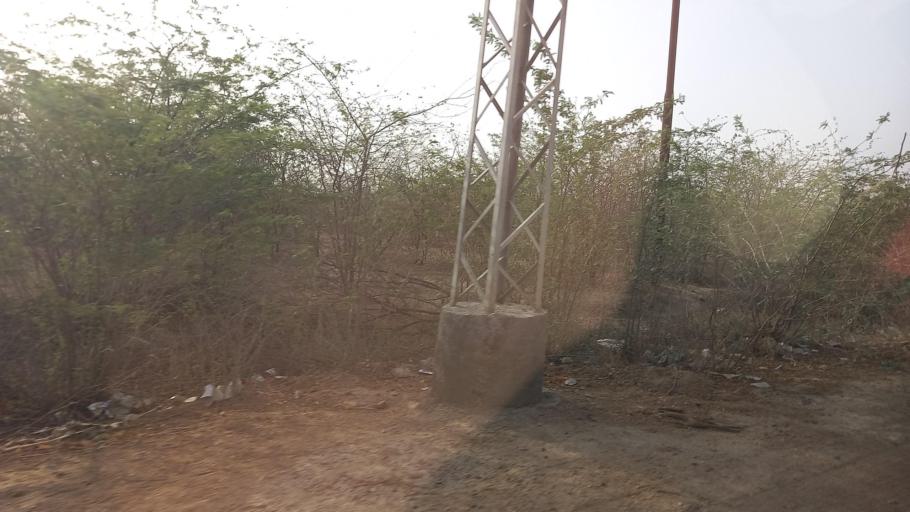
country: PK
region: Sindh
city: Malir Cantonment
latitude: 25.1155
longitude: 67.1916
